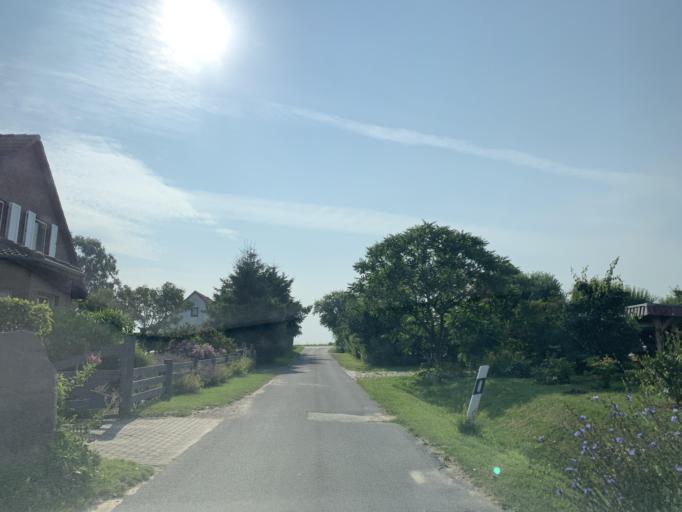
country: DE
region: Mecklenburg-Vorpommern
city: Gross Nemerow
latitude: 53.4218
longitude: 13.1989
